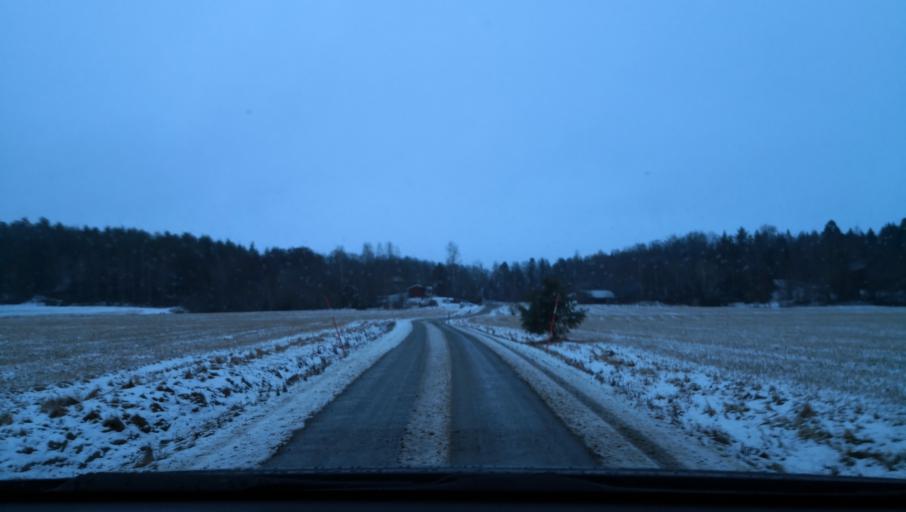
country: SE
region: Vaestmanland
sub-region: Kungsors Kommun
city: Kungsoer
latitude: 59.3992
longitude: 16.2054
